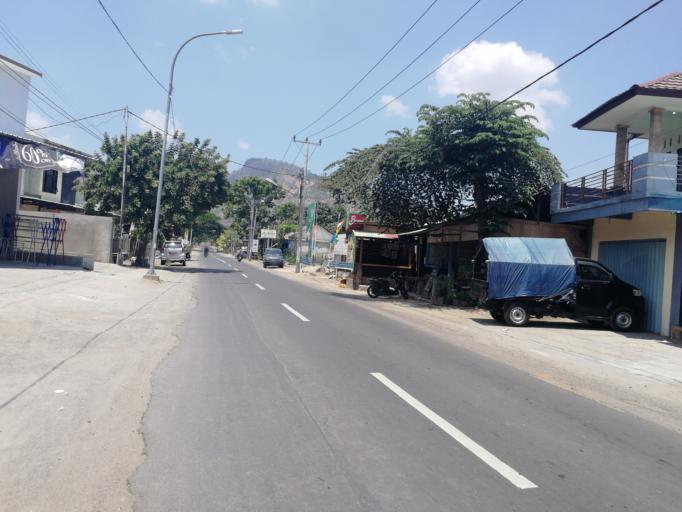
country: ID
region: West Nusa Tenggara
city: Karangsubagan
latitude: -8.4078
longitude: 116.1020
